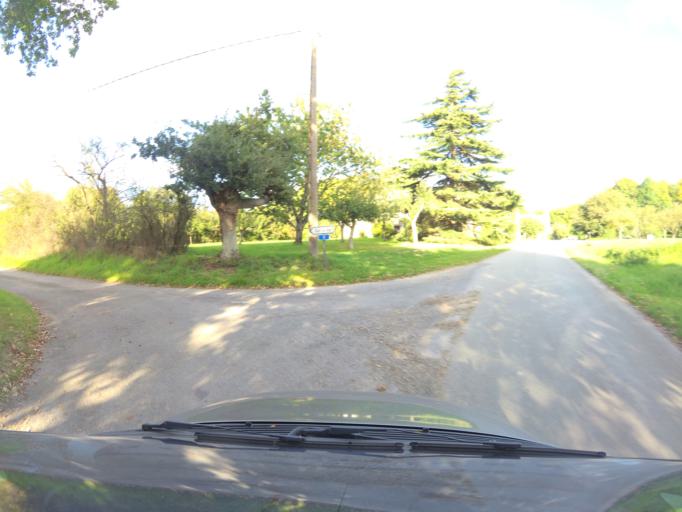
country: FR
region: Brittany
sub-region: Departement du Morbihan
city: Peillac
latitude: 47.7219
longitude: -2.1974
